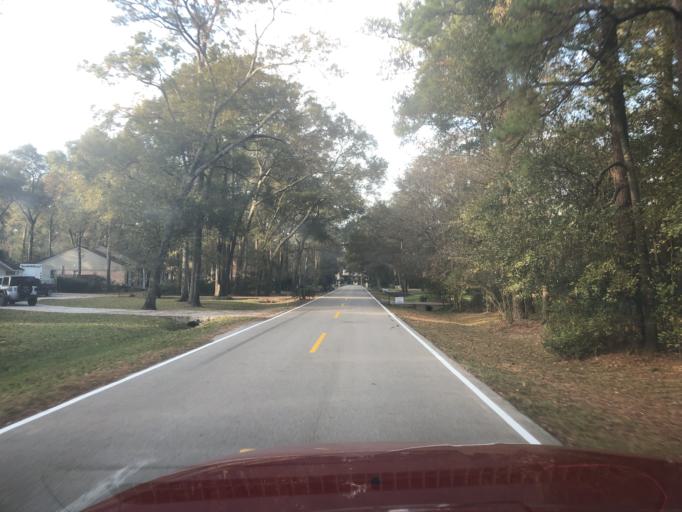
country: US
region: Texas
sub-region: Harris County
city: Spring
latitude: 30.0200
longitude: -95.4761
